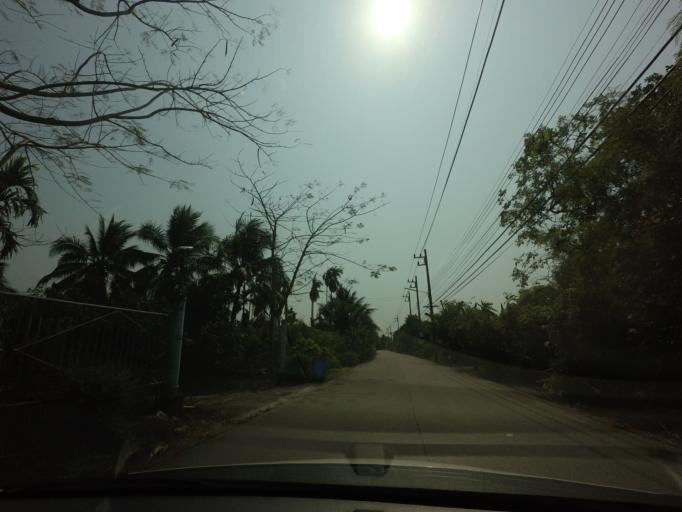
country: TH
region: Nakhon Pathom
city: Sam Phran
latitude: 13.7628
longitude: 100.2602
